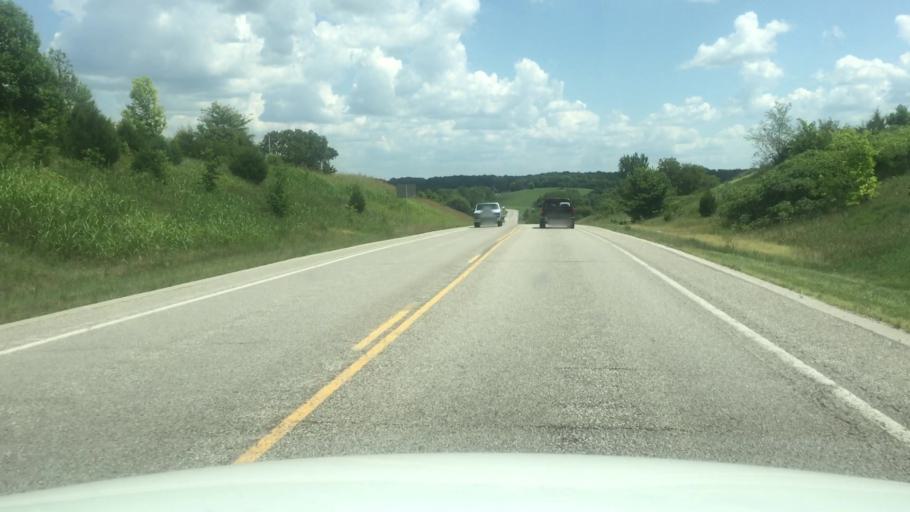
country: US
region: Missouri
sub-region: Platte County
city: Weston
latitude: 39.3921
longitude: -94.8470
